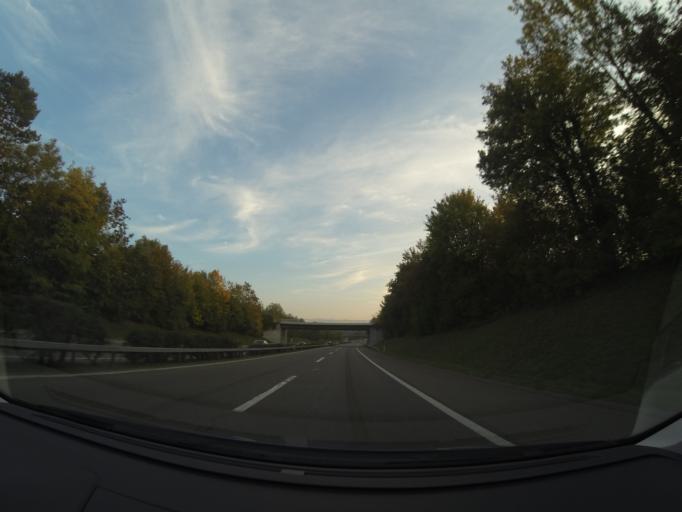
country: CH
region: Zurich
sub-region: Bezirk Hinwil
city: Durnten
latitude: 47.2692
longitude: 8.8321
